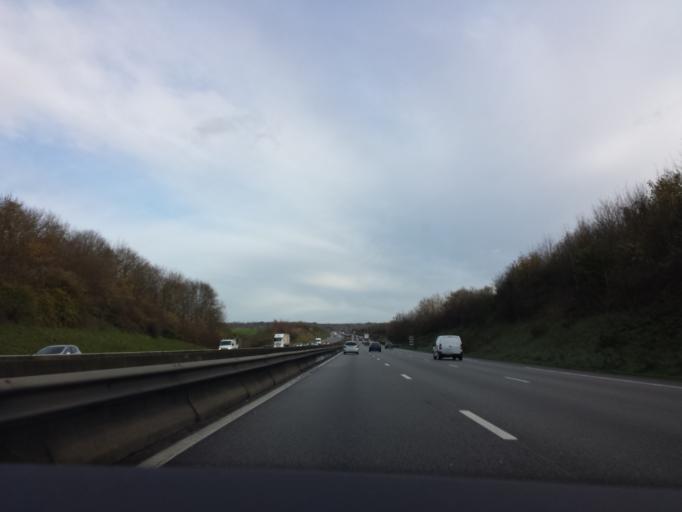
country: FR
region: Ile-de-France
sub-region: Departement des Yvelines
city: Bailly
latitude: 48.8212
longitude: 2.0696
